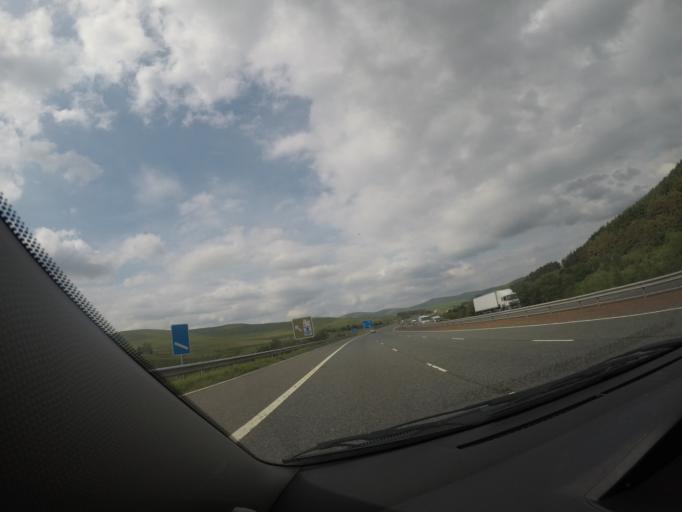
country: GB
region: Scotland
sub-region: South Lanarkshire
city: Biggar
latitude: 55.4452
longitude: -3.6527
